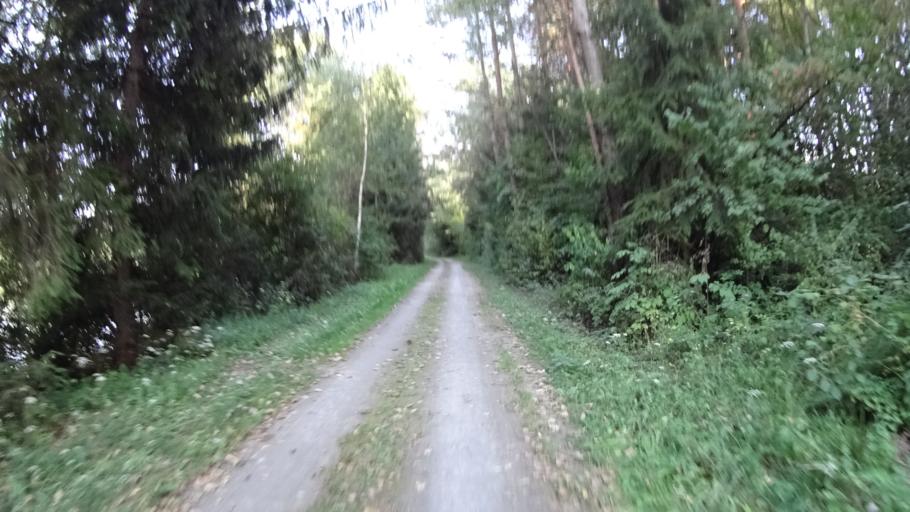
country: AT
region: Carinthia
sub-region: Politischer Bezirk Villach Land
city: Rosegg
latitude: 46.5718
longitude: 14.0518
